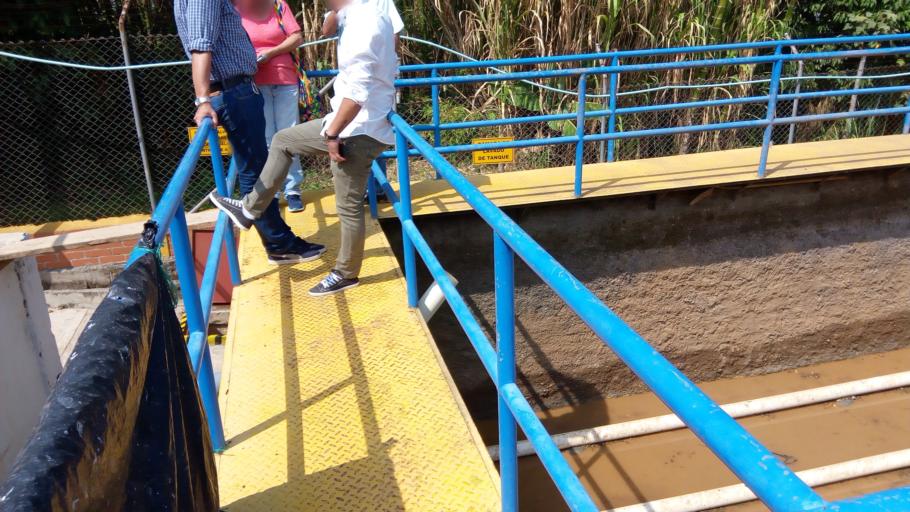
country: CO
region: Valle del Cauca
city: Cali
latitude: 3.4699
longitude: -76.5516
